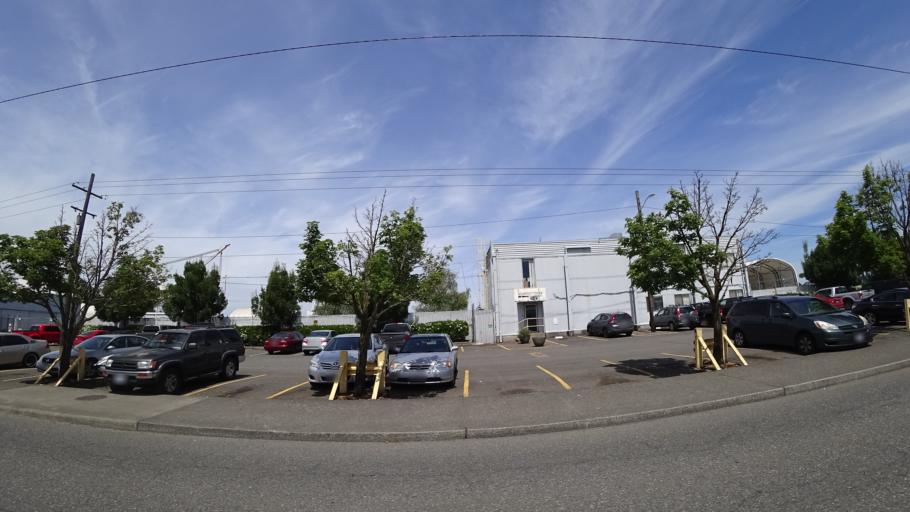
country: US
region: Oregon
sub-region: Multnomah County
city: Portland
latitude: 45.5527
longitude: -122.7172
